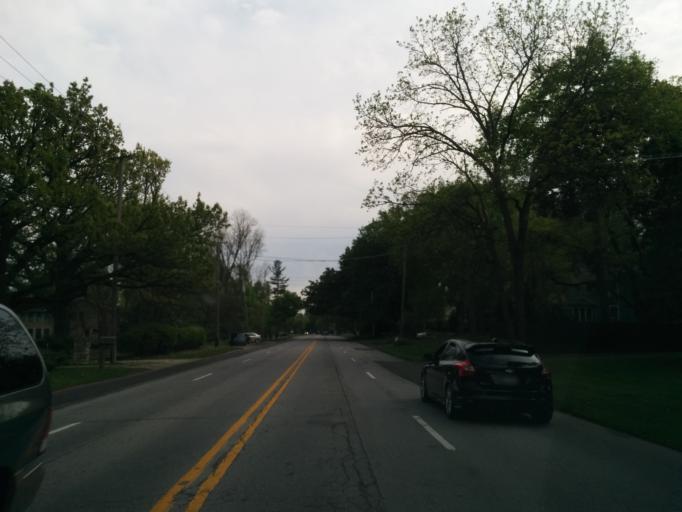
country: US
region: Illinois
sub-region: Kane County
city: North Aurora
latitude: 41.8147
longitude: -88.3279
